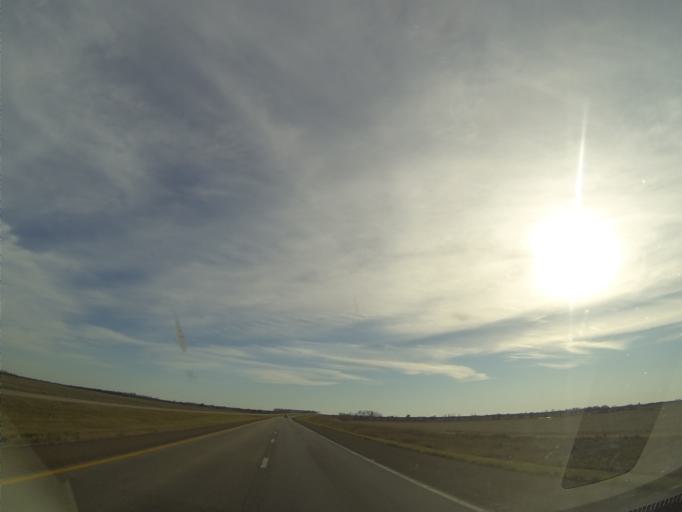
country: US
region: Kansas
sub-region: Ottawa County
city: Minneapolis
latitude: 39.0797
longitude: -97.6498
